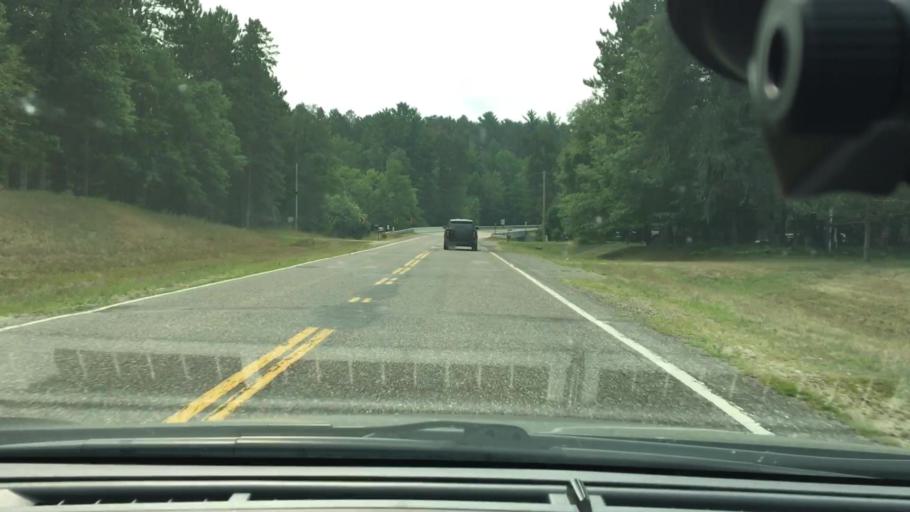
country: US
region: Minnesota
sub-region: Crow Wing County
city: Cross Lake
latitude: 46.6547
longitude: -94.0989
